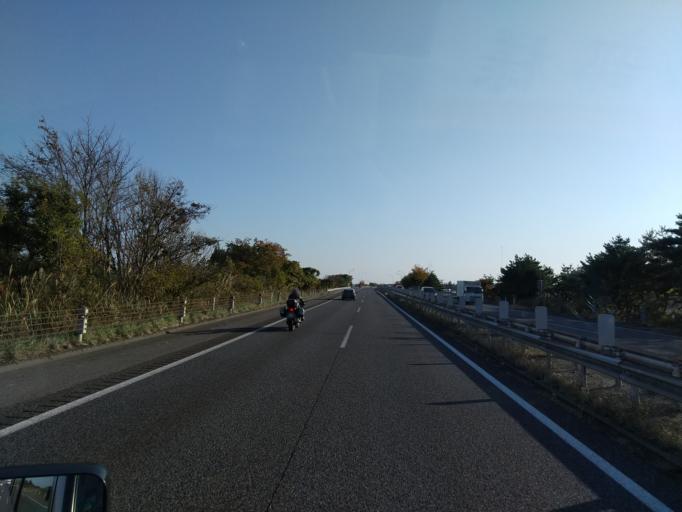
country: JP
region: Iwate
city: Morioka-shi
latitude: 39.6245
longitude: 141.1289
